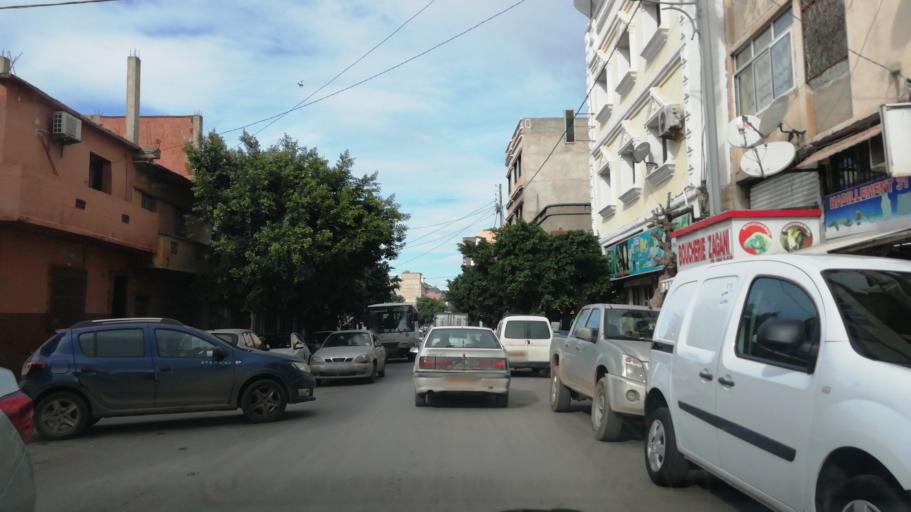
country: DZ
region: Oran
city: Oran
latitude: 35.6891
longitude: -0.6235
